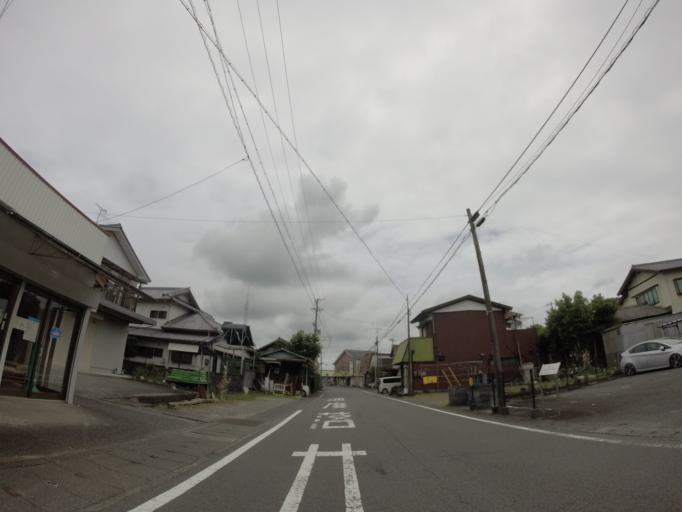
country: JP
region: Shizuoka
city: Shimada
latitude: 34.7684
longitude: 138.1846
